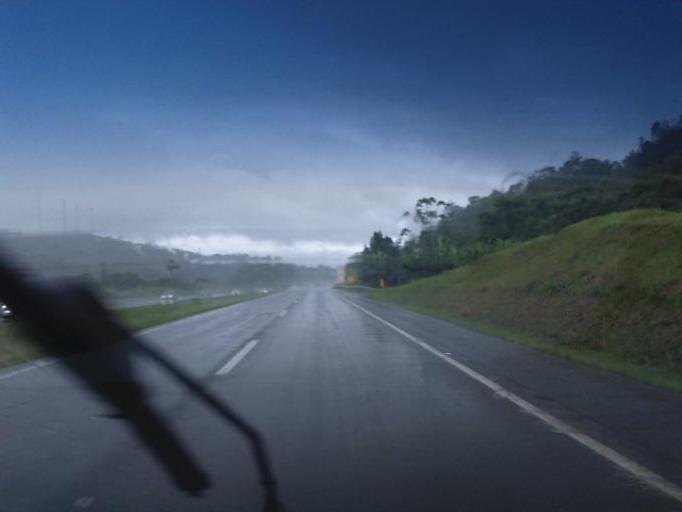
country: BR
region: Sao Paulo
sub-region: Miracatu
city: Miracatu
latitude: -24.2667
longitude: -47.3913
